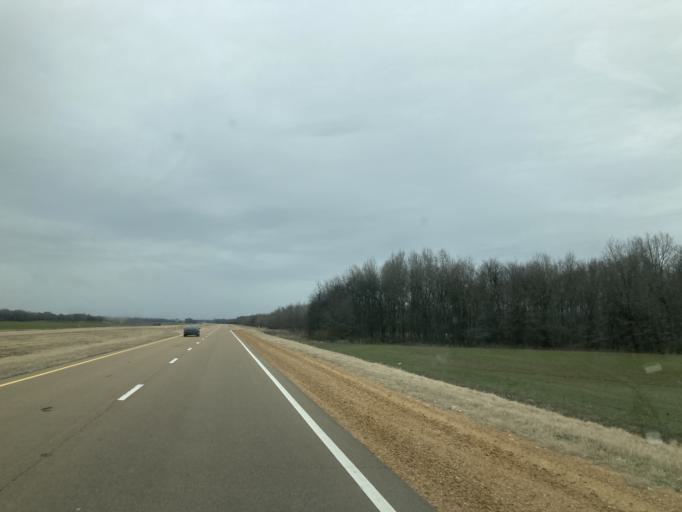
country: US
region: Mississippi
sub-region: Yazoo County
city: Yazoo City
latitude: 33.0128
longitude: -90.4690
